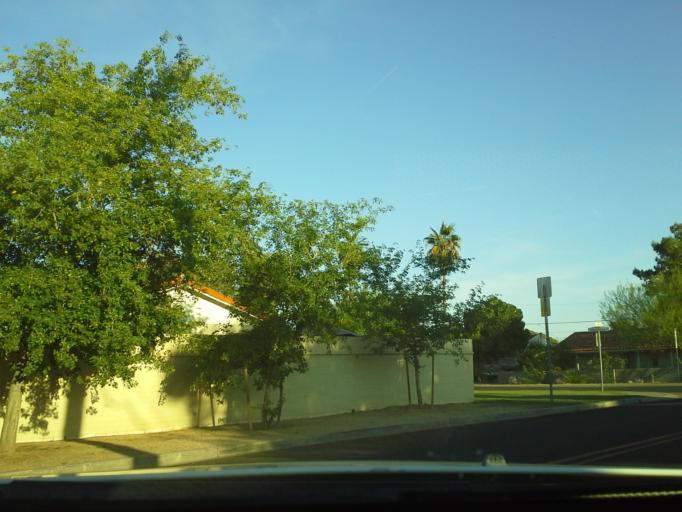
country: US
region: Arizona
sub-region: Maricopa County
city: Phoenix
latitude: 33.5087
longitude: -112.0694
